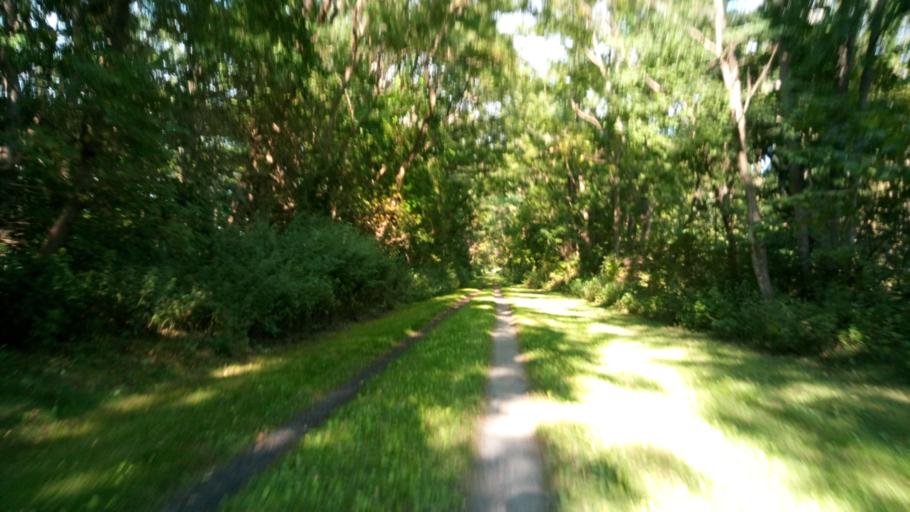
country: US
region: New York
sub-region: Monroe County
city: Honeoye Falls
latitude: 42.9904
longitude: -77.5358
